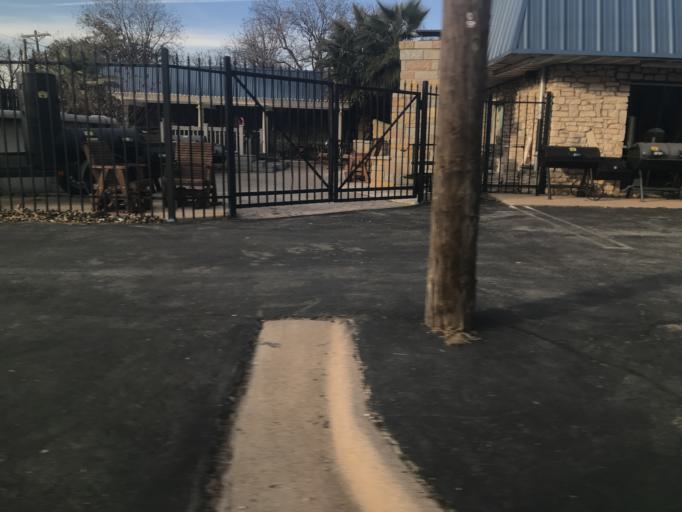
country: US
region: Texas
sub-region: Taylor County
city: Abilene
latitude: 32.4323
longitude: -99.7516
